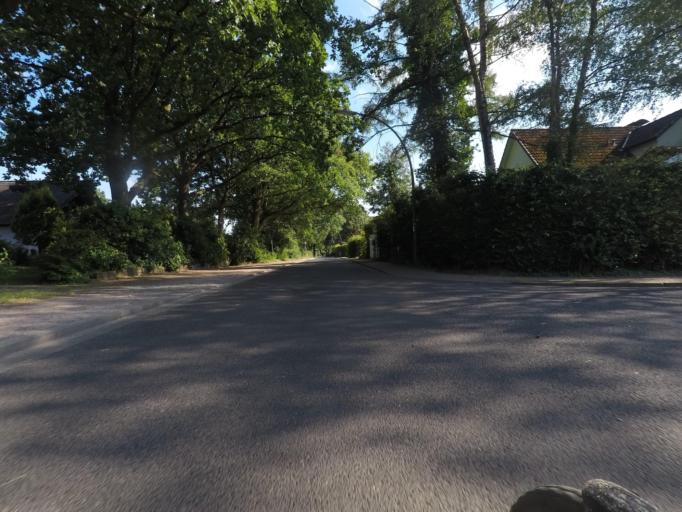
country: DE
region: Hamburg
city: Sasel
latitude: 53.6399
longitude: 10.1179
